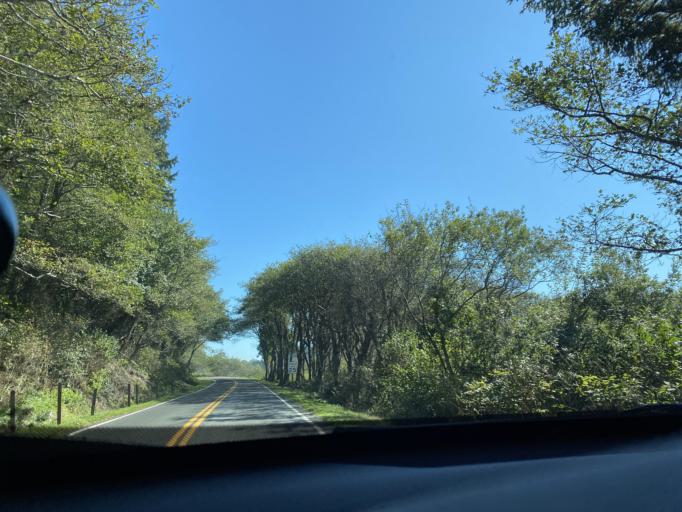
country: US
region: Washington
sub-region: Clallam County
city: Forks
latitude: 47.9205
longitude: -124.6372
